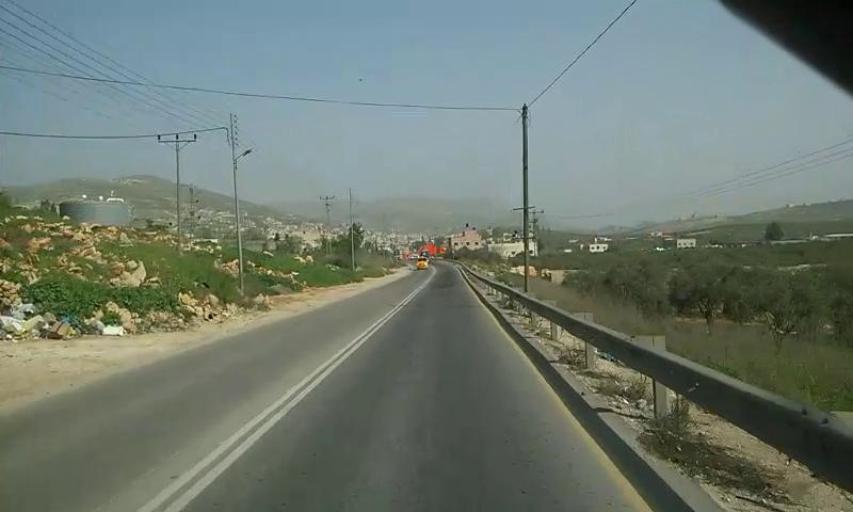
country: PS
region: West Bank
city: Huwwarah
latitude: 32.1340
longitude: 35.2580
